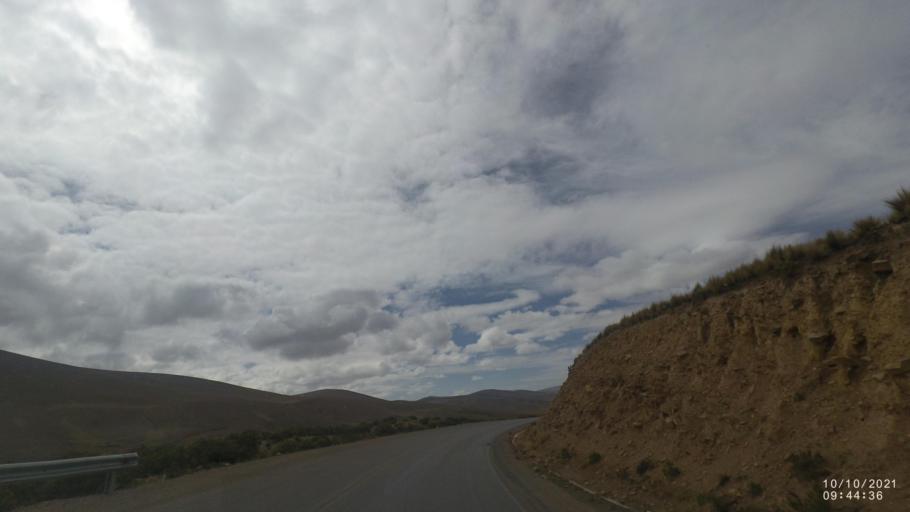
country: BO
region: La Paz
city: Quime
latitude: -17.1615
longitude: -67.3358
